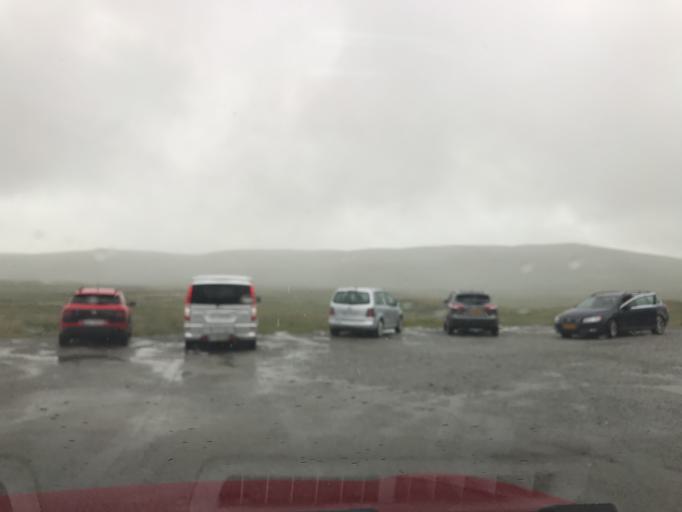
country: NO
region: Buskerud
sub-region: Hol
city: Geilo
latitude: 60.5494
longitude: 8.0689
